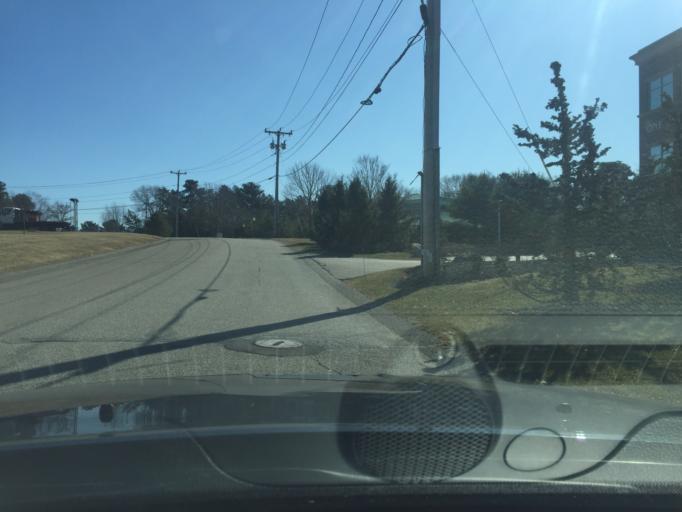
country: US
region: Massachusetts
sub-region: Plymouth County
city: North Plymouth
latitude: 41.9498
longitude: -70.7085
